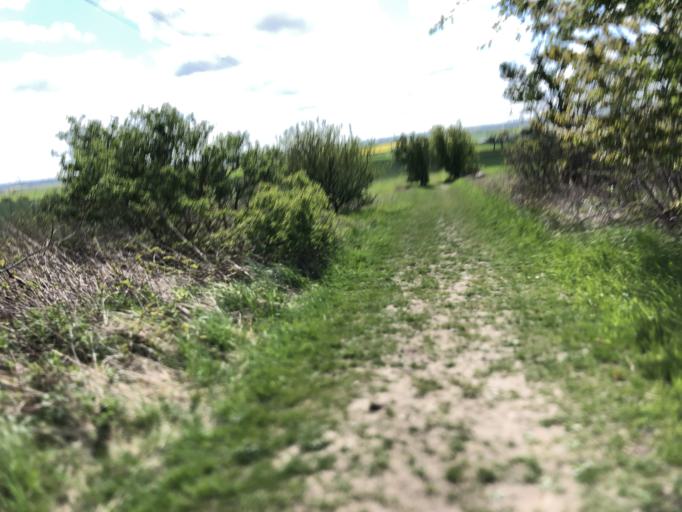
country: SE
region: Skane
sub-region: Lunds Kommun
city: Lund
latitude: 55.6949
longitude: 13.2872
